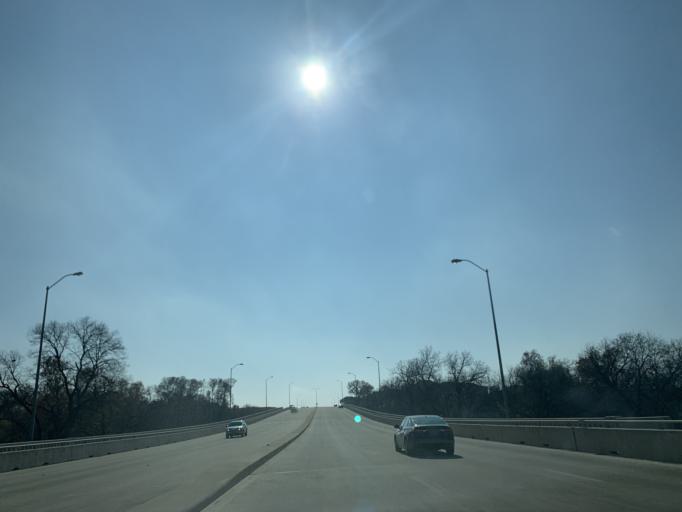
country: US
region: Texas
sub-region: Williamson County
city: Round Rock
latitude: 30.5145
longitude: -97.6366
